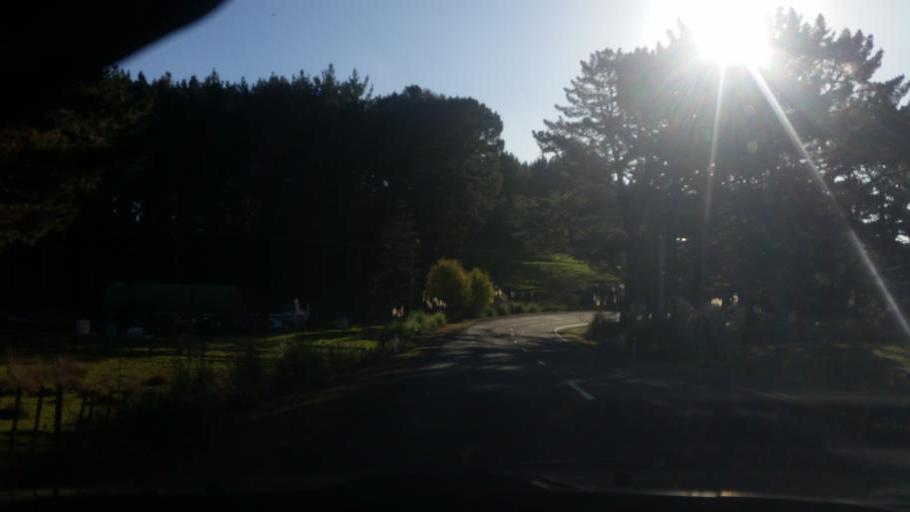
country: NZ
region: Northland
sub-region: Kaipara District
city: Dargaville
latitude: -36.2195
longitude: 174.0377
